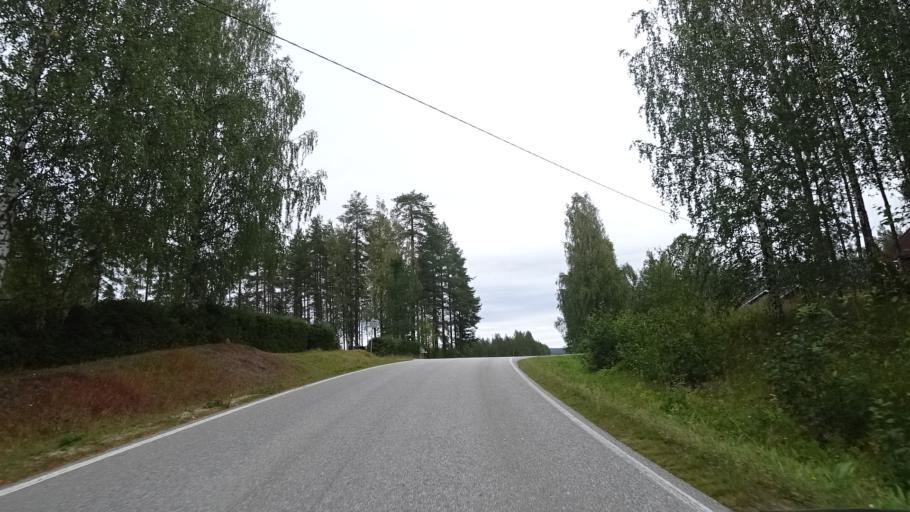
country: FI
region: North Karelia
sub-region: Pielisen Karjala
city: Lieksa
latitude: 63.3752
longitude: 30.3053
